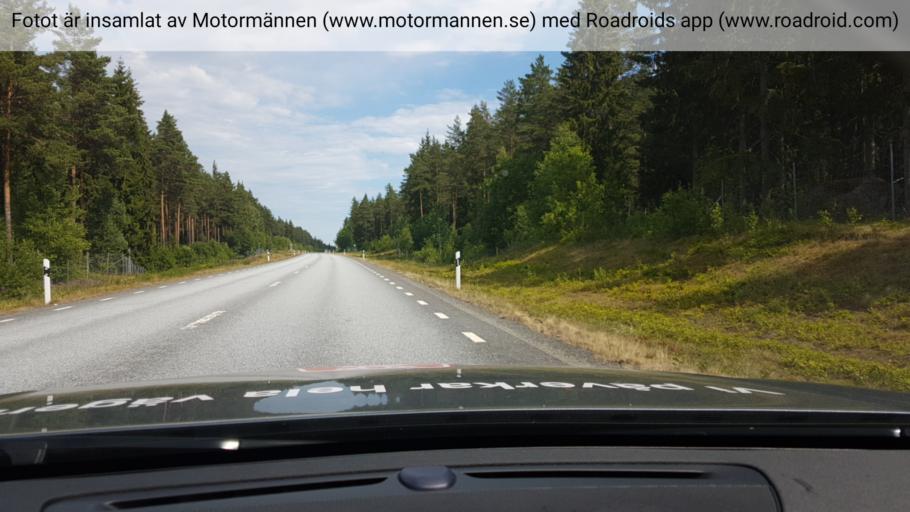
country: SE
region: Uppsala
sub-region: Osthammars Kommun
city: Gimo
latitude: 60.1649
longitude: 18.2571
